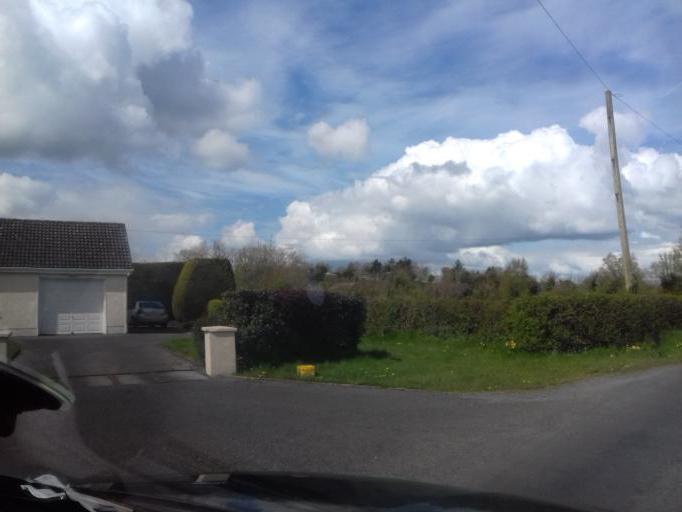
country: GB
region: Northern Ireland
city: Lisnaskea
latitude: 54.1912
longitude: -7.5136
